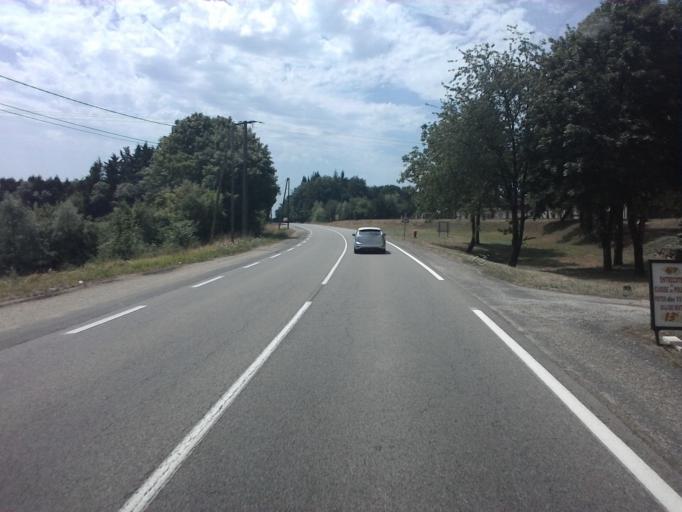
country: FR
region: Rhone-Alpes
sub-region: Departement de l'Ain
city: Coligny
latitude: 46.3616
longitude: 5.3298
